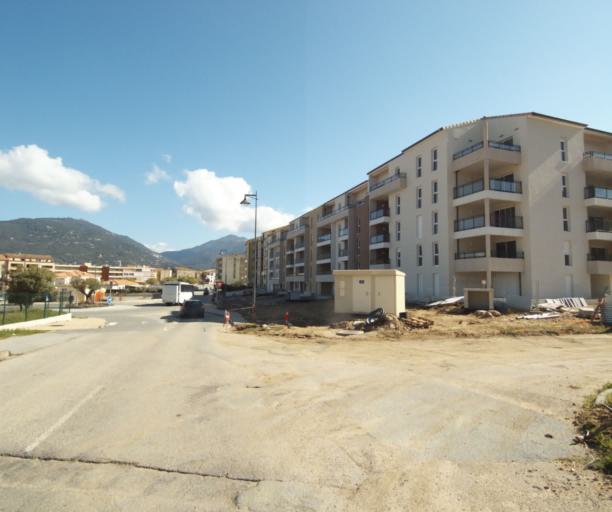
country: FR
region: Corsica
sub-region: Departement de la Corse-du-Sud
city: Propriano
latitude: 41.6726
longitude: 8.9010
